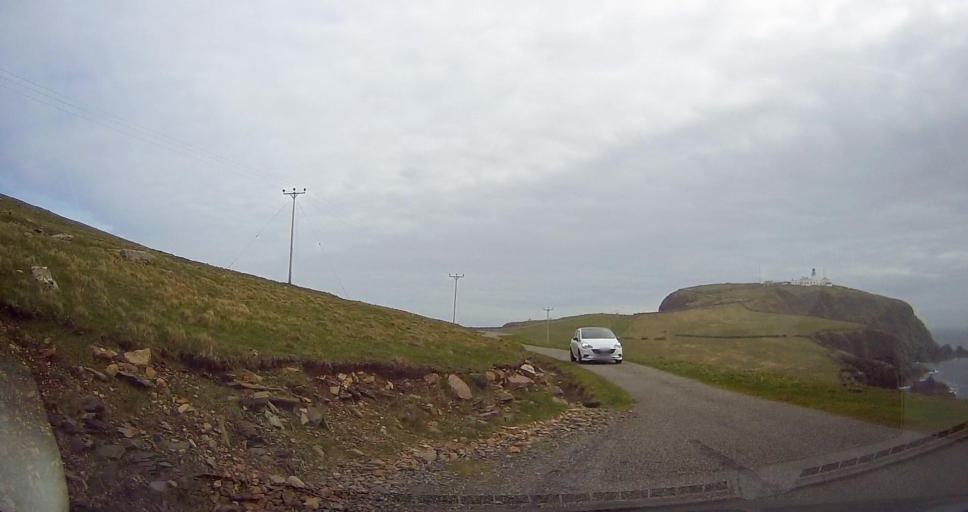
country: GB
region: Scotland
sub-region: Shetland Islands
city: Sandwick
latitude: 59.8597
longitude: -1.2776
